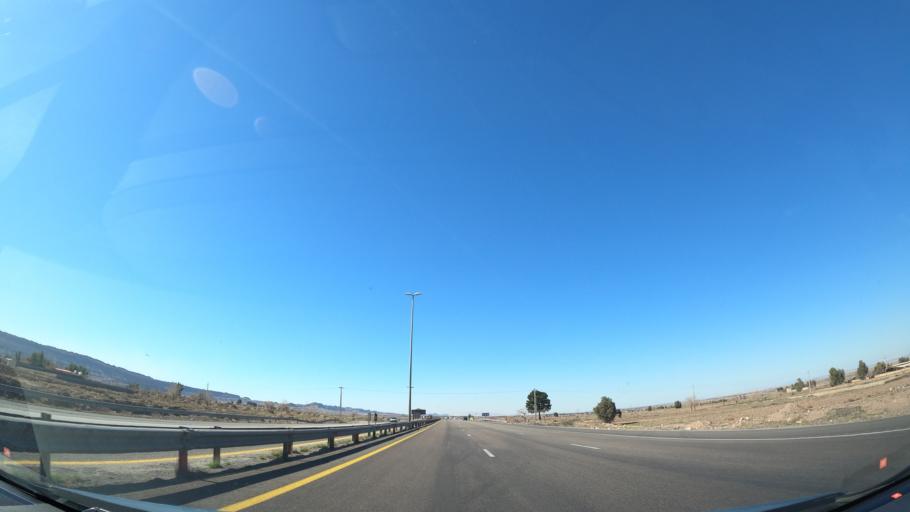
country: IR
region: Qom
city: Qom
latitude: 34.4631
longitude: 51.0854
